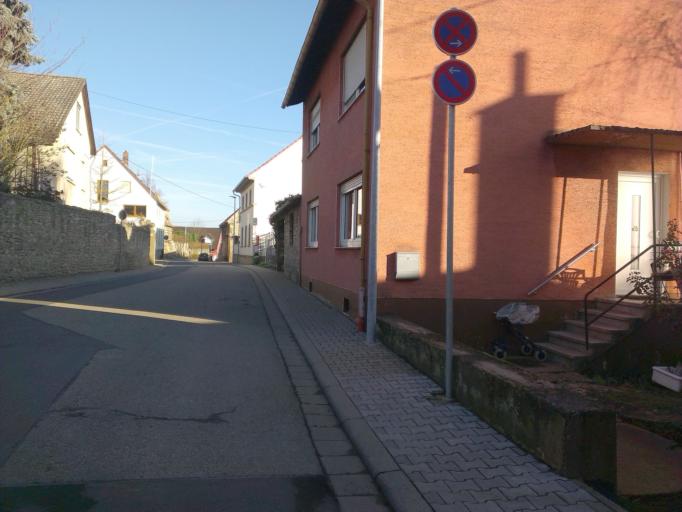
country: DE
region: Rheinland-Pfalz
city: Molsheim
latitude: 49.6461
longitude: 8.1653
